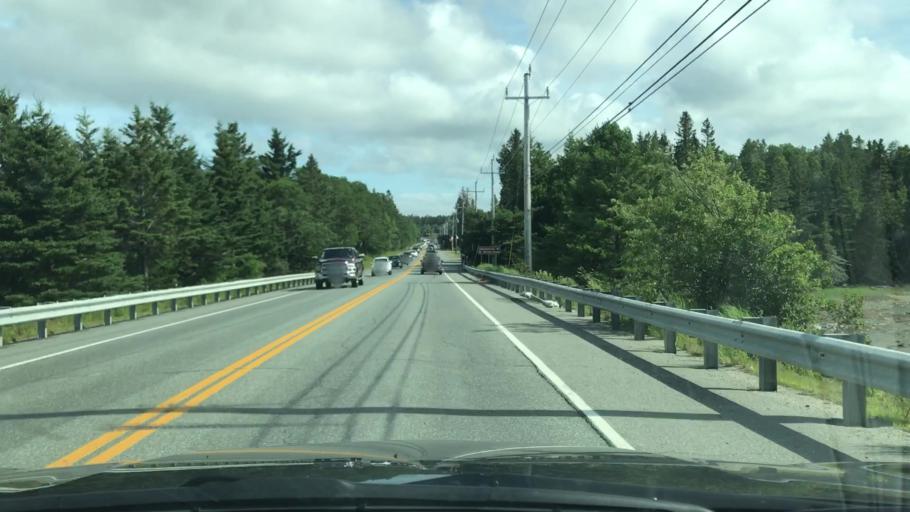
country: US
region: Maine
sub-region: Hancock County
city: Trenton
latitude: 44.4290
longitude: -68.3671
